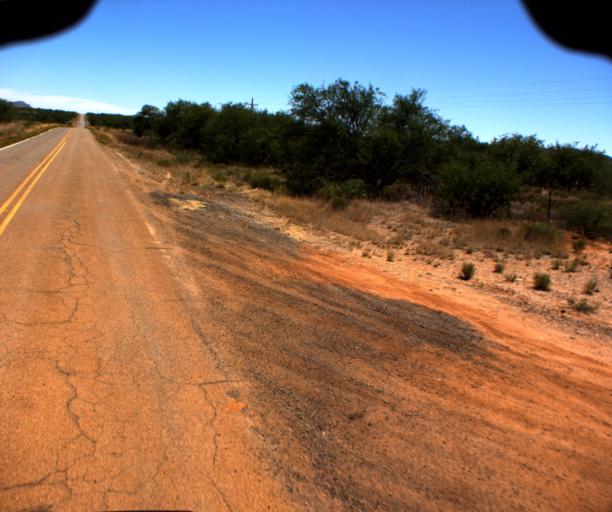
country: US
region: Arizona
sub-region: Santa Cruz County
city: Tubac
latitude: 31.5415
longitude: -111.5404
